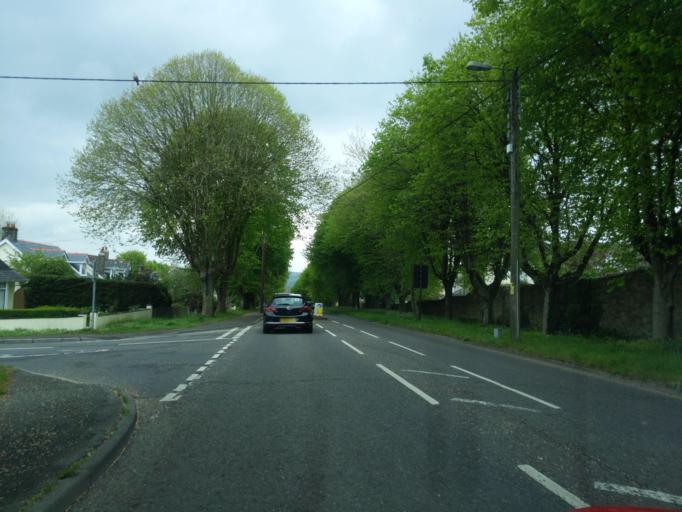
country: GB
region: England
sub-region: Cornwall
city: Bodmin
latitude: 50.4682
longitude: -4.7371
